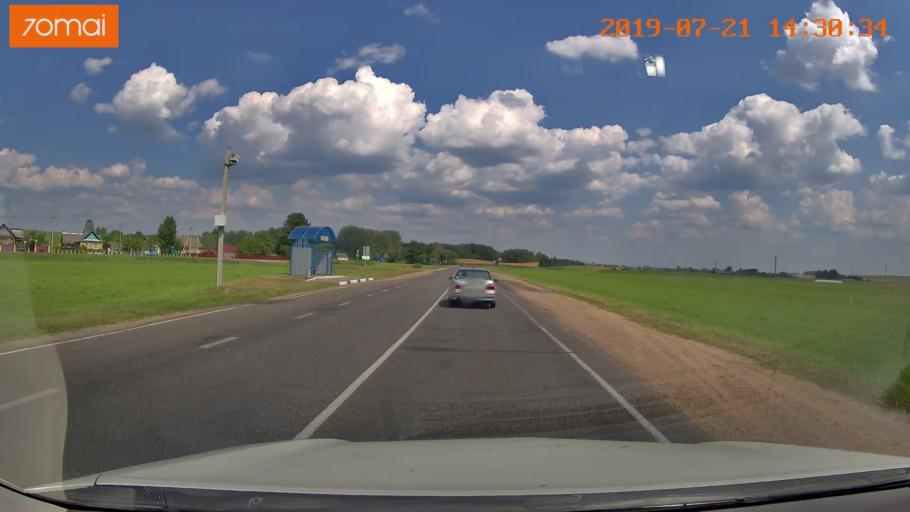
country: BY
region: Grodnenskaya
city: Karelichy
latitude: 53.5240
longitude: 26.2754
